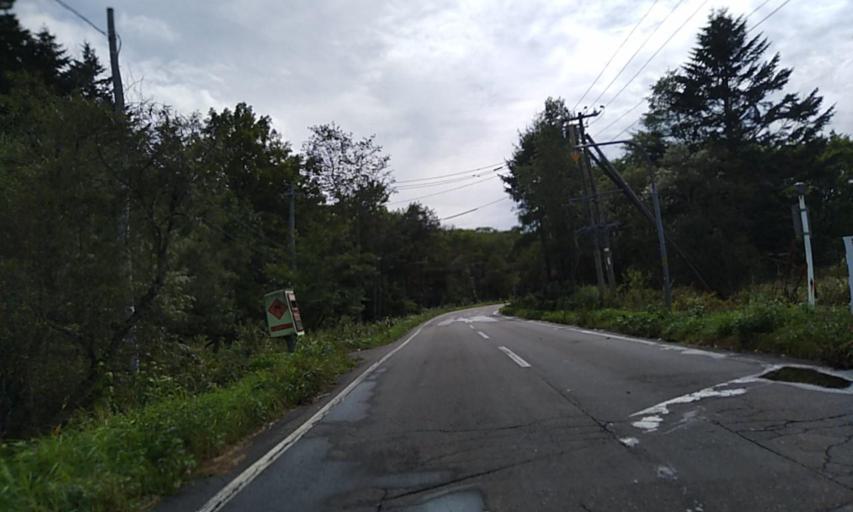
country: JP
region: Hokkaido
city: Kushiro
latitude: 42.8436
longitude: 143.8421
